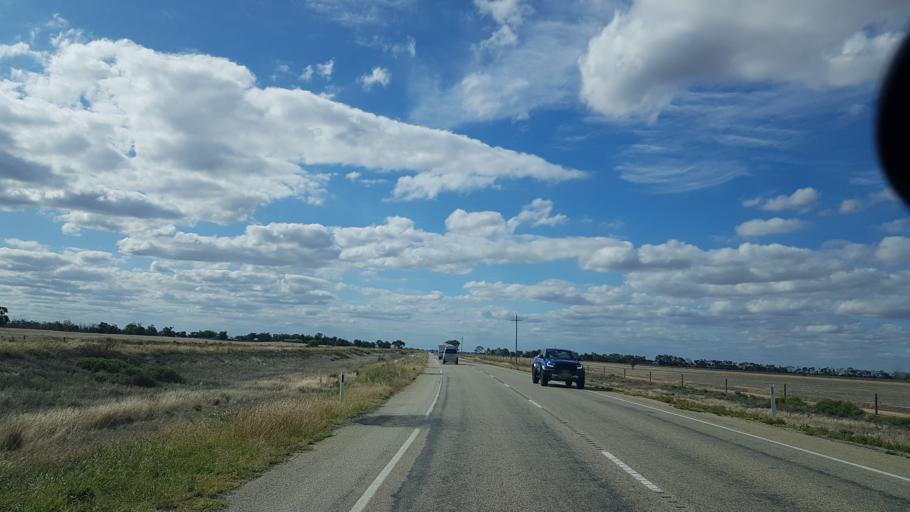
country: AU
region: Victoria
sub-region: Swan Hill
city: Swan Hill
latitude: -35.8110
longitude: 143.9561
